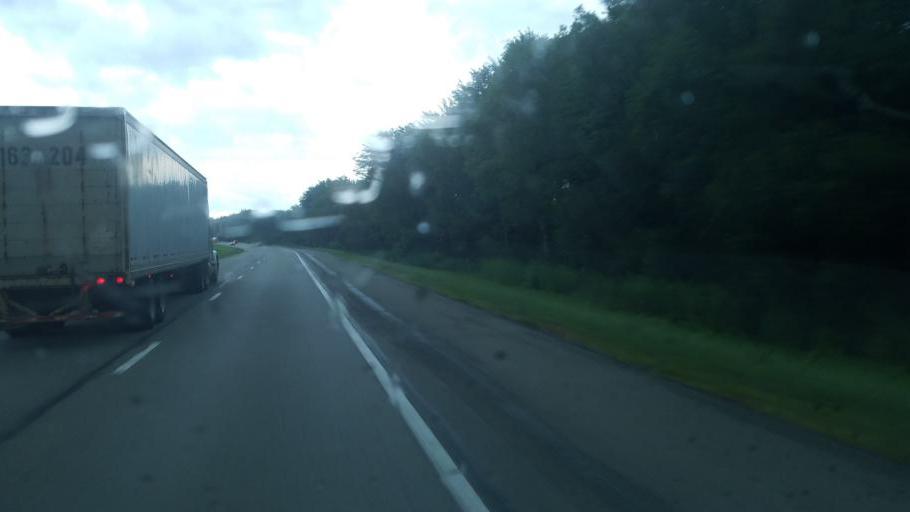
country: US
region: Pennsylvania
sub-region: Mercer County
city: Grove City
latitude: 41.0906
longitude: -80.1390
